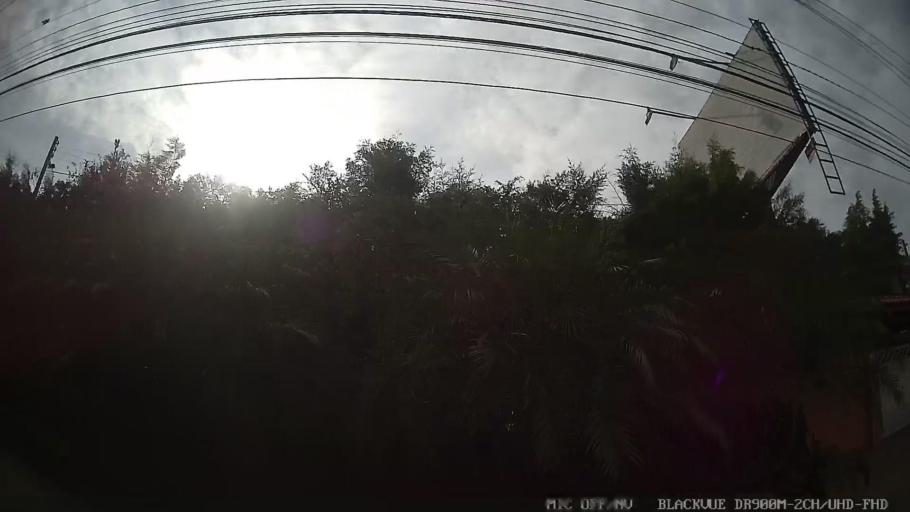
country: BR
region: Sao Paulo
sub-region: Indaiatuba
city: Indaiatuba
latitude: -23.1018
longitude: -47.1833
